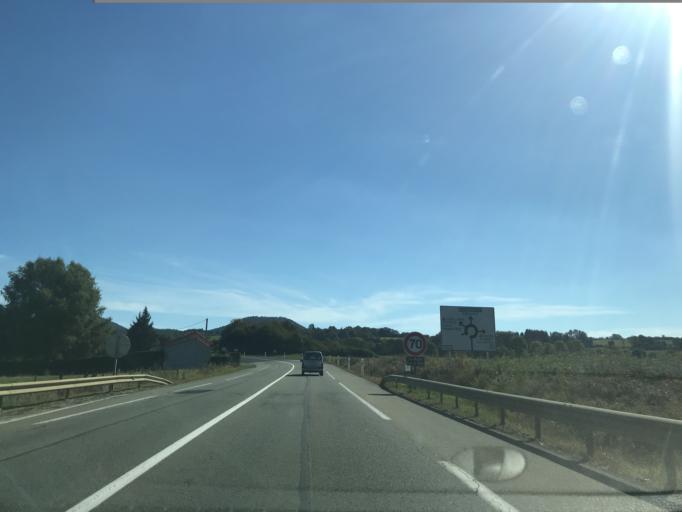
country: FR
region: Auvergne
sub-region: Departement du Puy-de-Dome
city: Aydat
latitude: 45.7285
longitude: 2.8855
